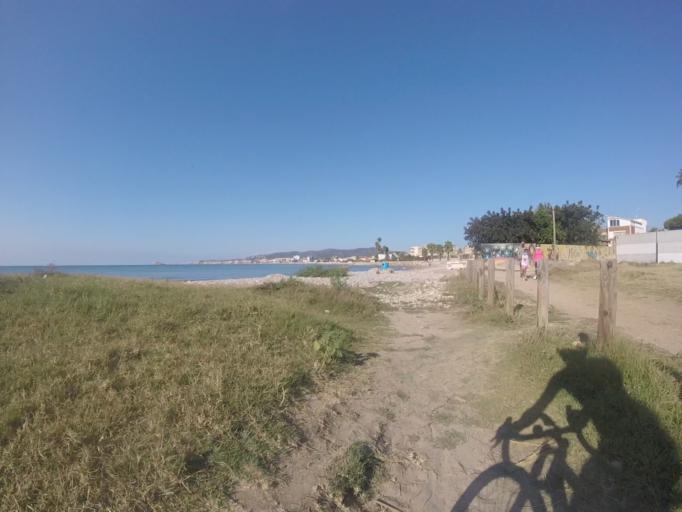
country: ES
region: Valencia
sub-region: Provincia de Castello
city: Benicarlo
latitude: 40.4095
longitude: 0.4281
